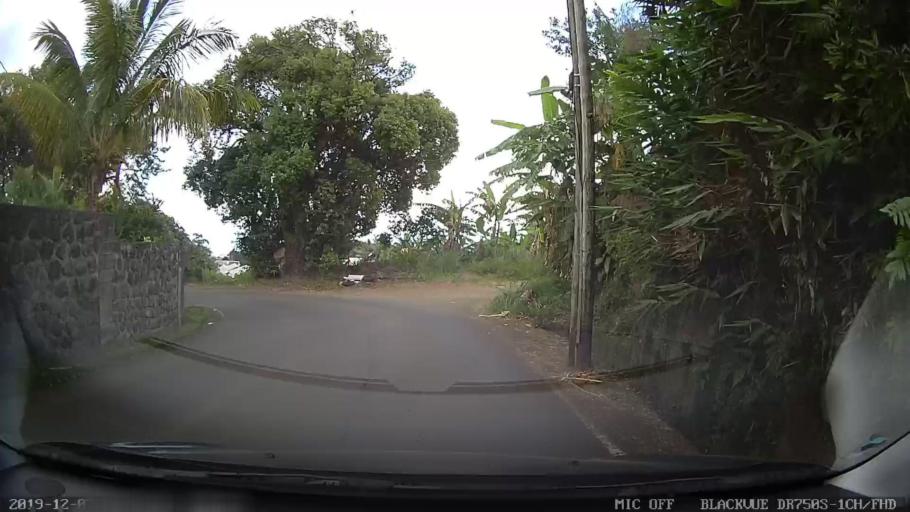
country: RE
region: Reunion
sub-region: Reunion
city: Sainte-Marie
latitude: -20.9360
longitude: 55.5341
